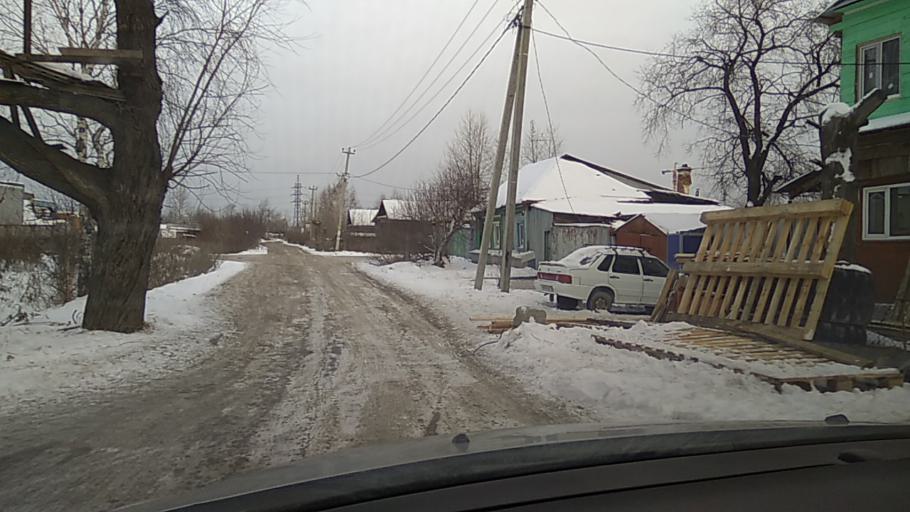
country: RU
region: Sverdlovsk
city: Shirokaya Rechka
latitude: 56.8326
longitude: 60.5278
